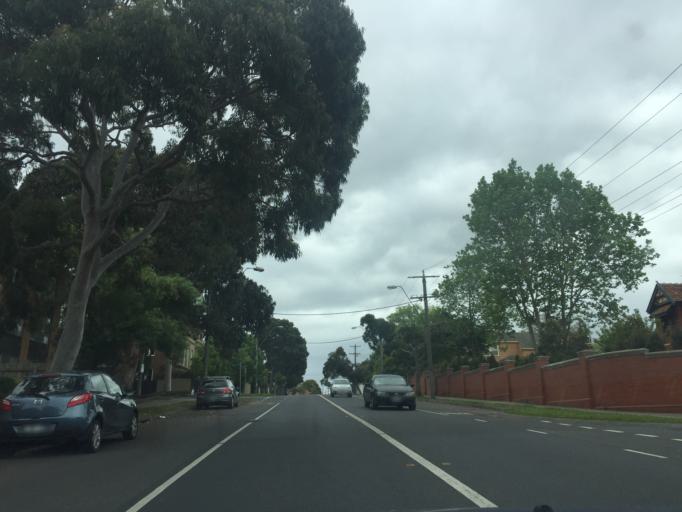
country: AU
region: Victoria
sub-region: Boroondara
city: Hawthorn East
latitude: -37.8179
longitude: 145.0459
